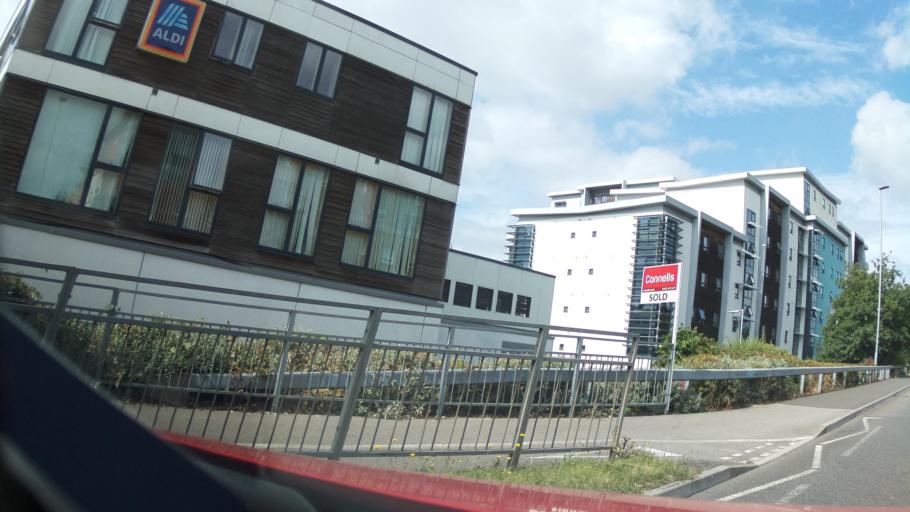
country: GB
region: England
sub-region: Poole
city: Poole
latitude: 50.7149
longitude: -1.9774
